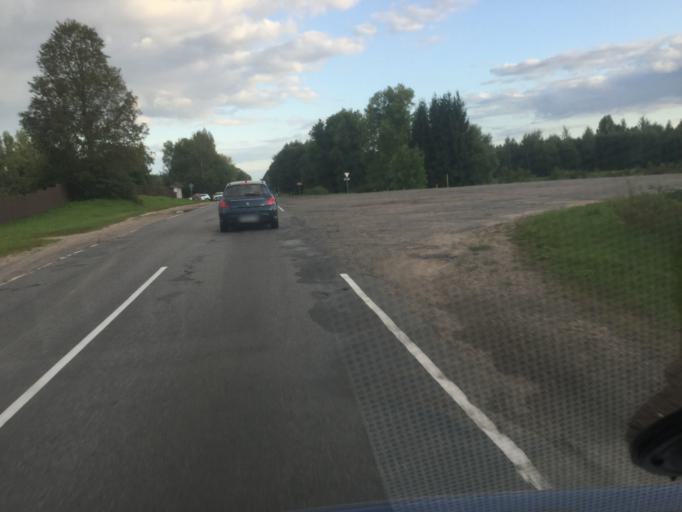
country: BY
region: Vitebsk
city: Navapolatsk
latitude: 55.5614
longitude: 28.6930
